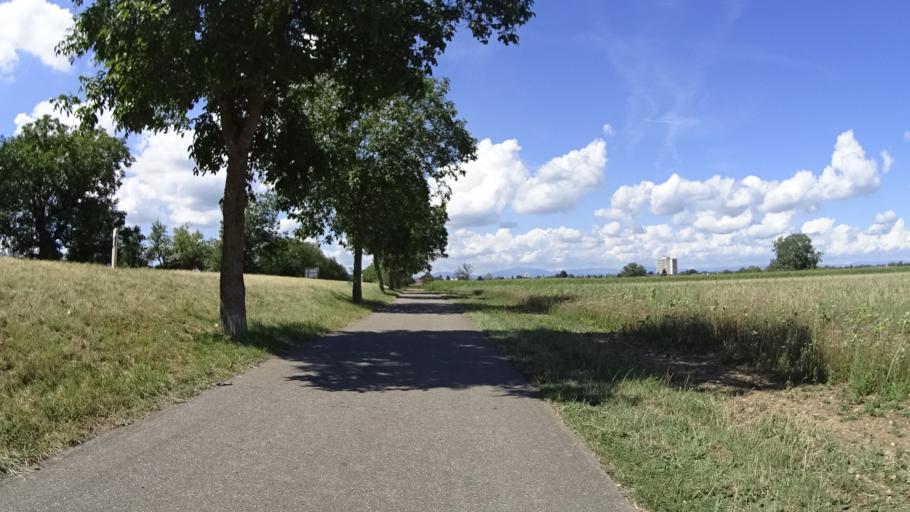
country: DE
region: Baden-Wuerttemberg
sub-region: Freiburg Region
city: Neuenburg am Rhein
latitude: 47.8114
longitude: 7.5798
